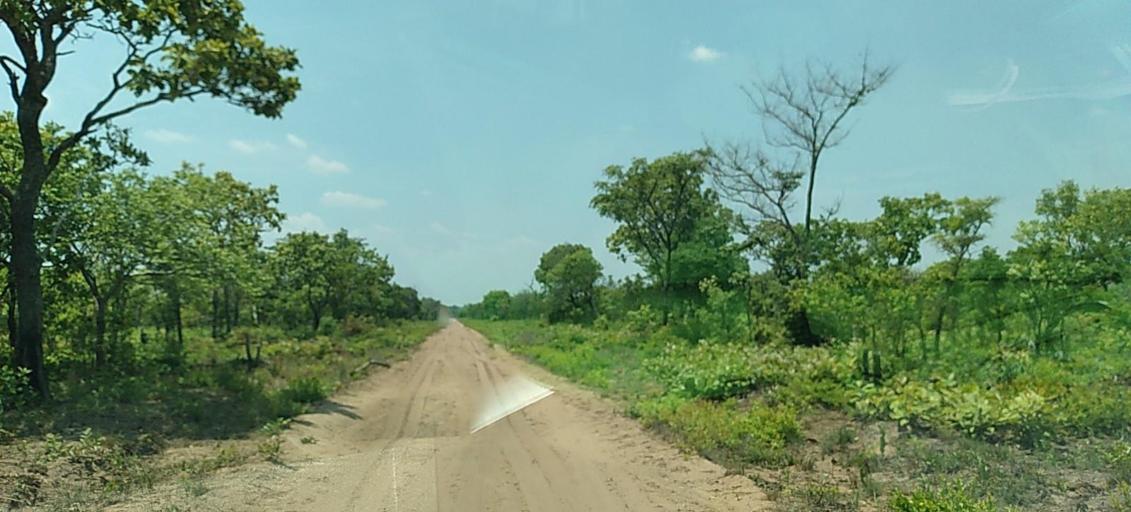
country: CD
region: Katanga
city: Kolwezi
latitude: -11.3383
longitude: 25.2217
